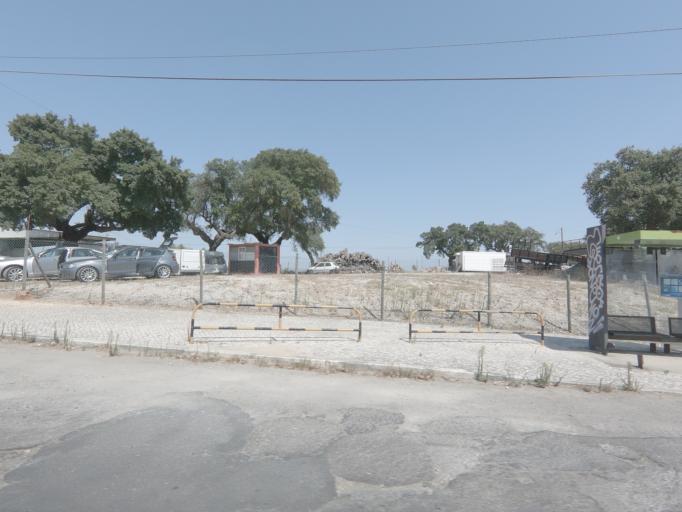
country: PT
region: Setubal
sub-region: Palmela
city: Palmela
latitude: 38.5659
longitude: -8.8876
